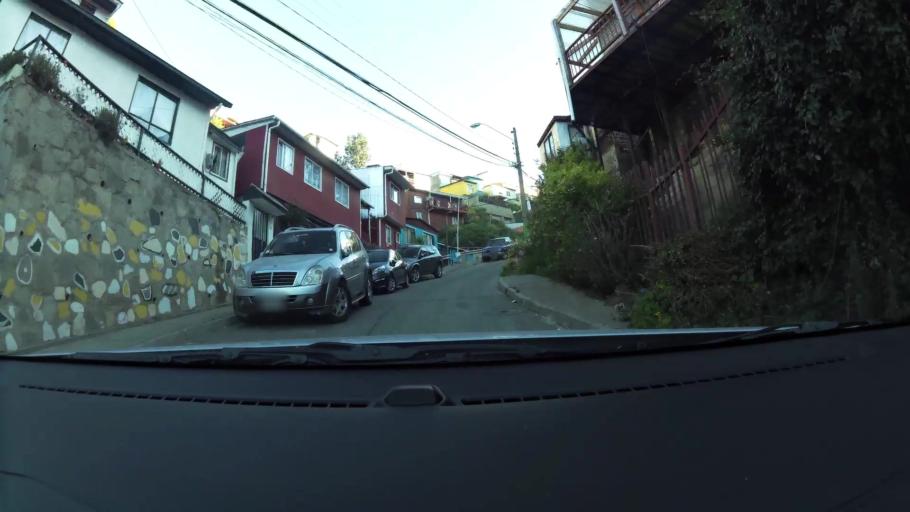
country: CL
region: Valparaiso
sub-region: Provincia de Valparaiso
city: Valparaiso
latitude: -33.0580
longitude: -71.6276
